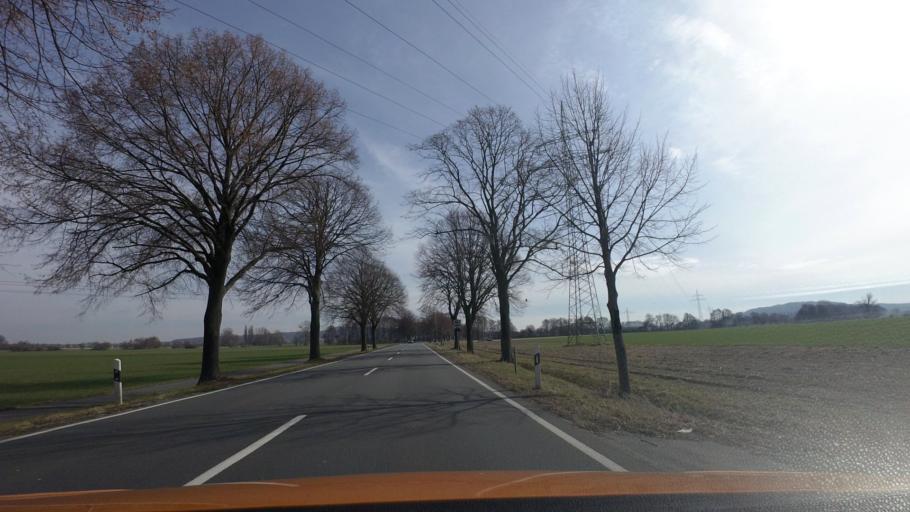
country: DE
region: Lower Saxony
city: Gehrden
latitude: 52.3402
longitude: 9.5598
